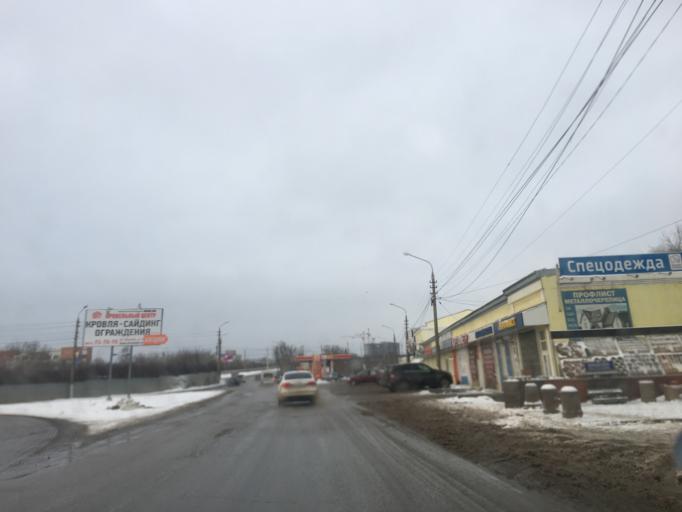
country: RU
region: Tula
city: Tula
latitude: 54.2034
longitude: 37.5901
